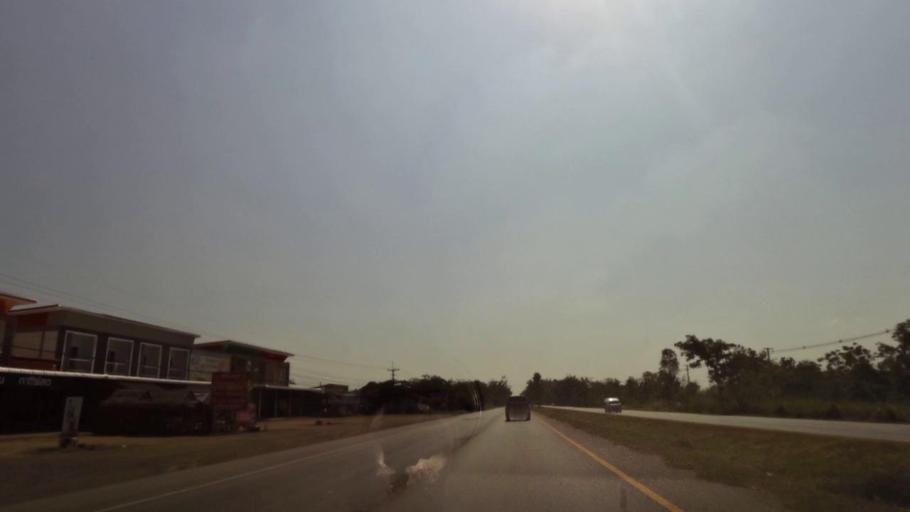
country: TH
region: Phichit
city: Bueng Na Rang
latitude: 16.3335
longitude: 100.1284
